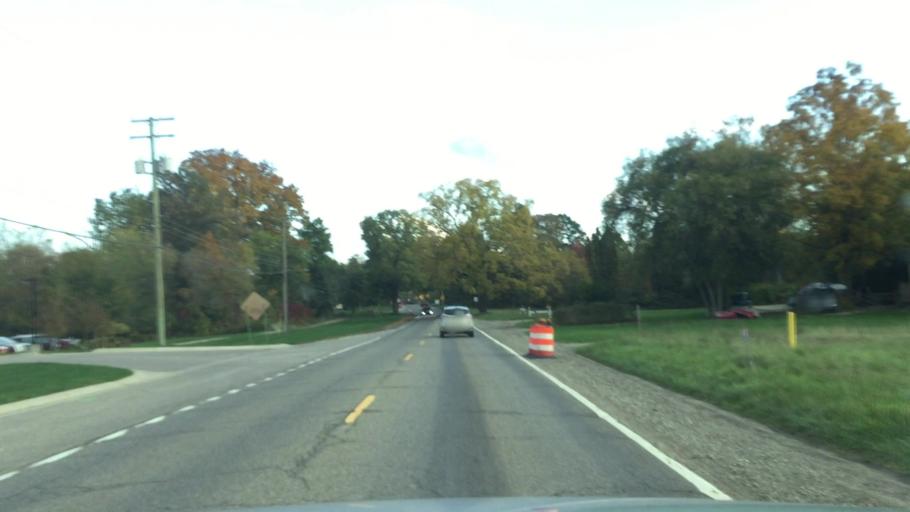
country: US
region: Michigan
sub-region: Oakland County
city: Wolverine Lake
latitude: 42.6444
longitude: -83.4993
